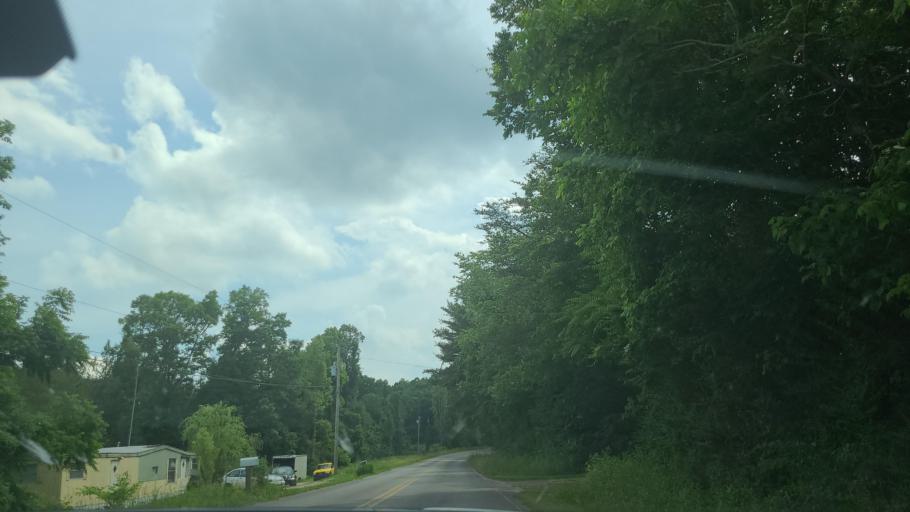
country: US
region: Tennessee
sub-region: Cumberland County
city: Lake Tansi
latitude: 35.7875
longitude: -85.0524
